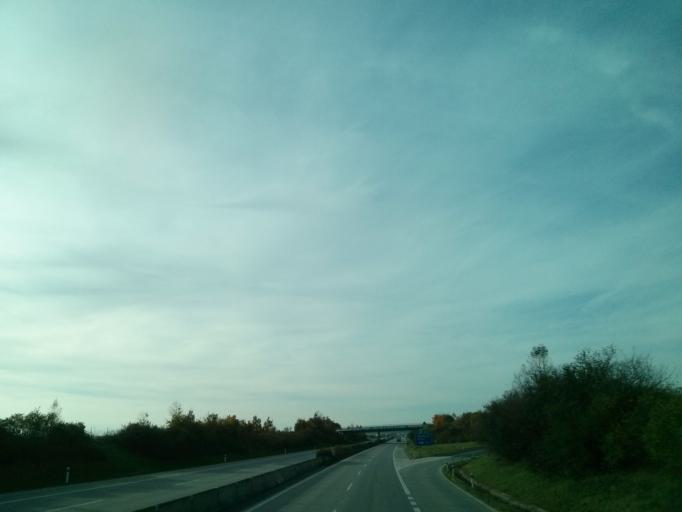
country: CZ
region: Plzensky
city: Hermanova Hut'
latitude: 49.7147
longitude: 13.1391
